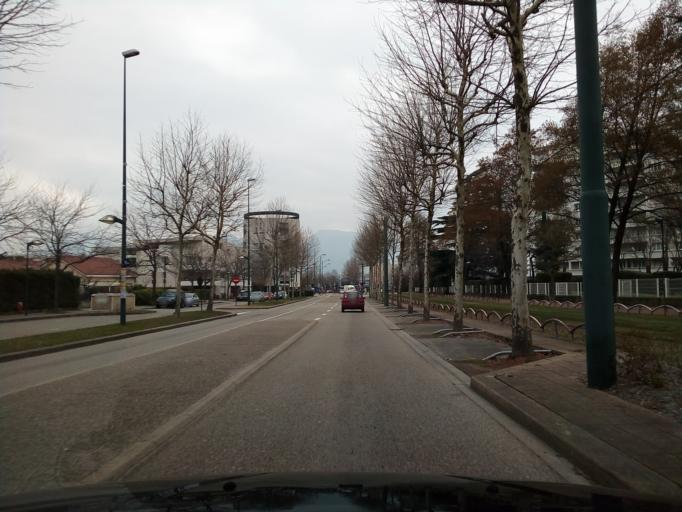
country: FR
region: Rhone-Alpes
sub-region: Departement de l'Isere
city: Echirolles
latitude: 45.1434
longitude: 5.7159
